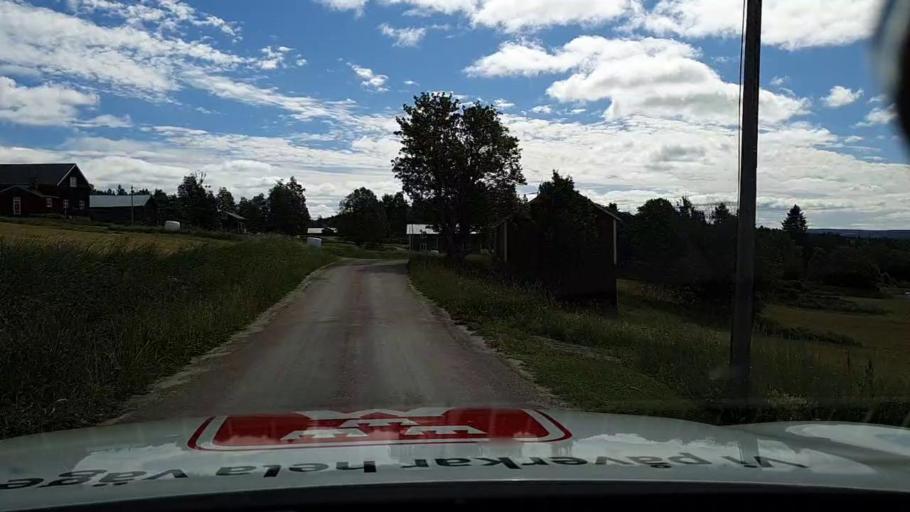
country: SE
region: Jaemtland
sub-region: Braecke Kommun
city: Braecke
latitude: 62.7658
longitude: 15.4961
